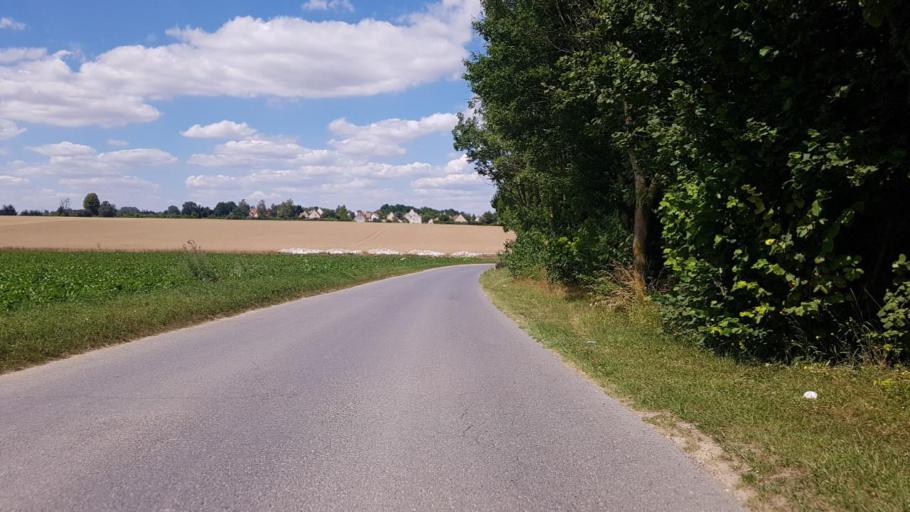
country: FR
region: Ile-de-France
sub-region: Departement de Seine-et-Marne
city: Claye-Souilly
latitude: 48.9847
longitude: 2.6686
